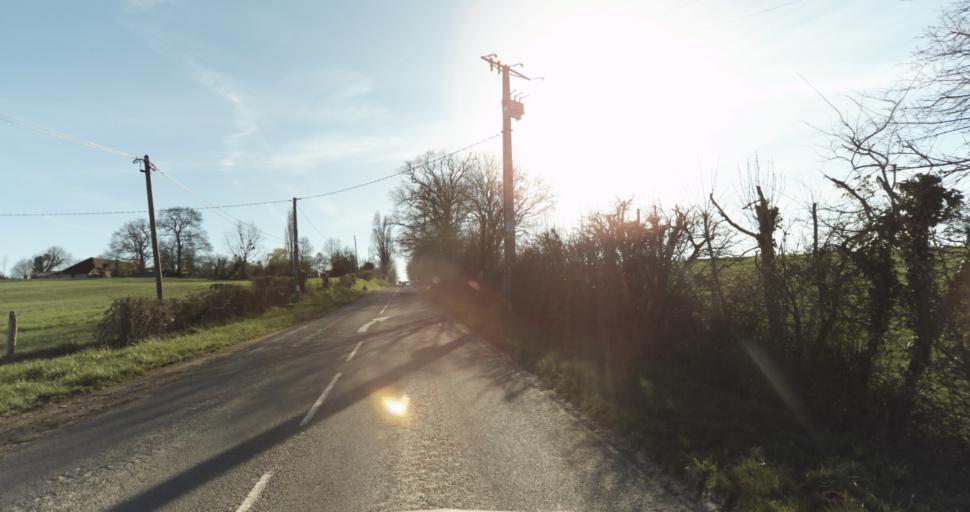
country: FR
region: Lower Normandy
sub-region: Departement du Calvados
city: Saint-Pierre-sur-Dives
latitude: 49.0320
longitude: 0.0005
